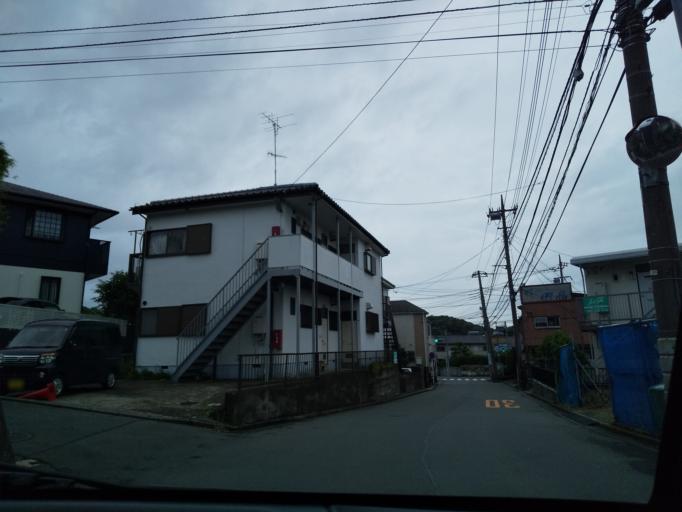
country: JP
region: Kanagawa
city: Fujisawa
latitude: 35.3923
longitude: 139.5099
